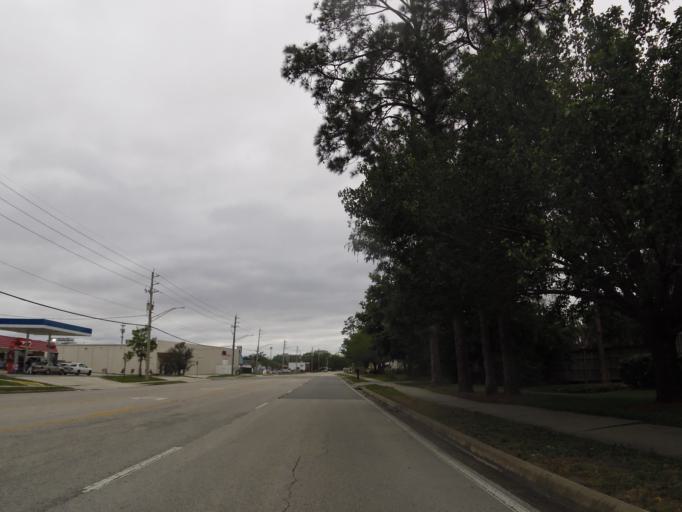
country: US
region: Florida
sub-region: Saint Johns County
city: Fruit Cove
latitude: 30.1999
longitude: -81.6152
